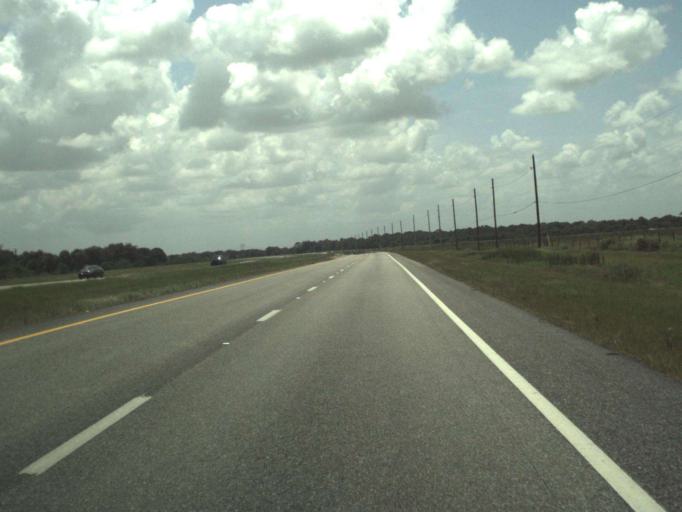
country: US
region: Florida
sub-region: Saint Lucie County
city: Fort Pierce South
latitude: 27.3743
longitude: -80.5678
